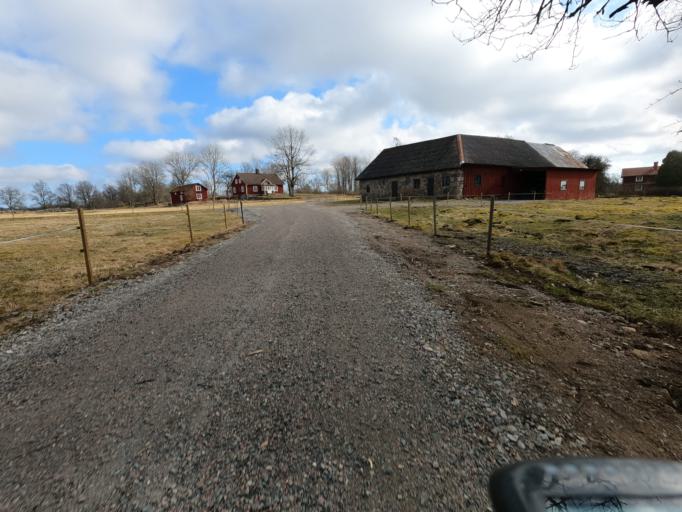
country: SE
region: Kronoberg
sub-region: Alvesta Kommun
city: Vislanda
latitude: 56.8180
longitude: 14.3603
